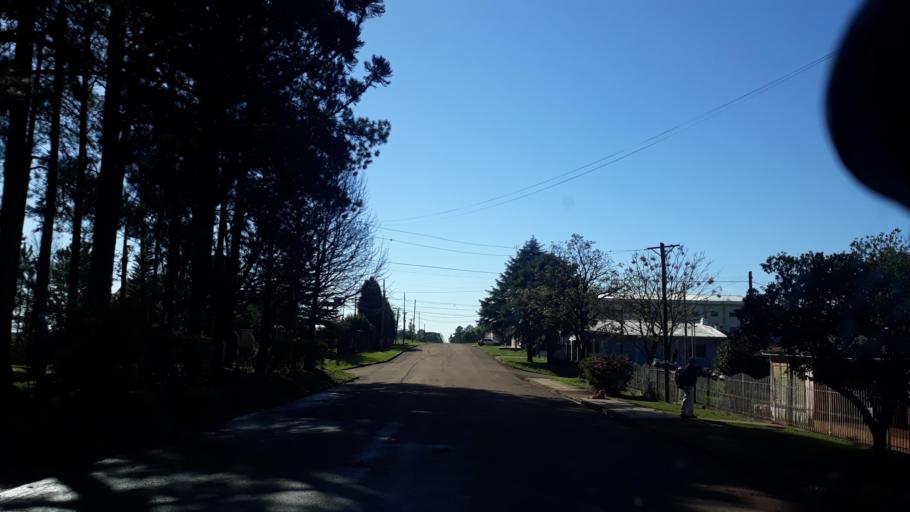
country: AR
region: Misiones
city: Bernardo de Irigoyen
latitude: -26.2637
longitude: -53.6511
